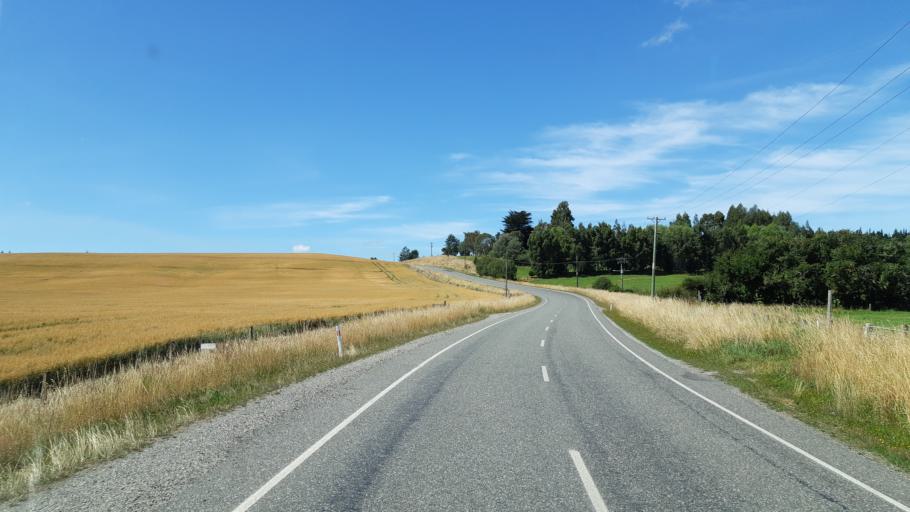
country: NZ
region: Southland
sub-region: Gore District
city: Gore
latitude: -46.0042
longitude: 168.8942
